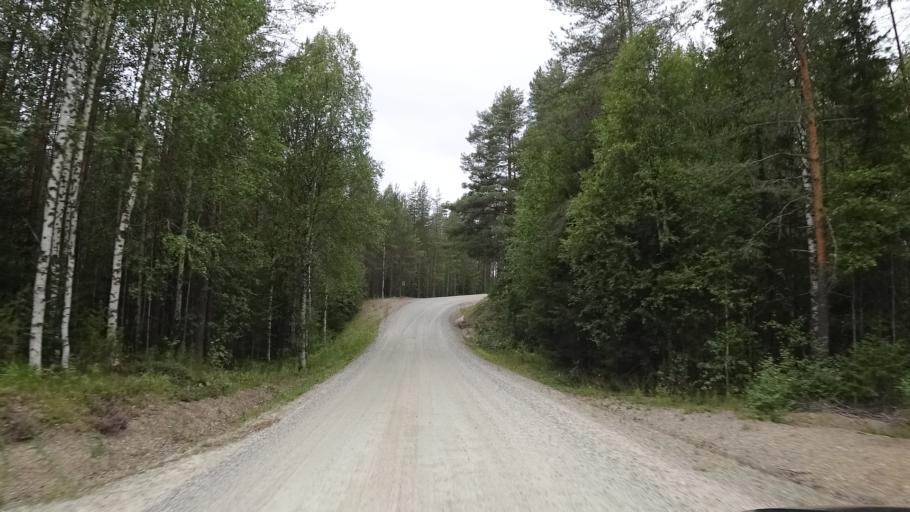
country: FI
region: North Karelia
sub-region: Pielisen Karjala
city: Lieksa
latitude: 63.2435
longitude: 30.3449
